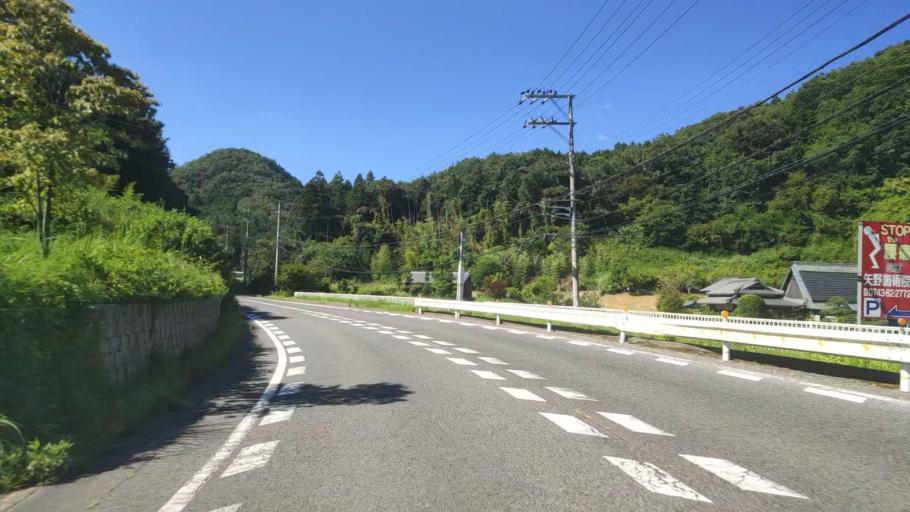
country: JP
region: Nara
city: Haibara-akanedai
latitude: 34.5824
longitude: 135.9698
